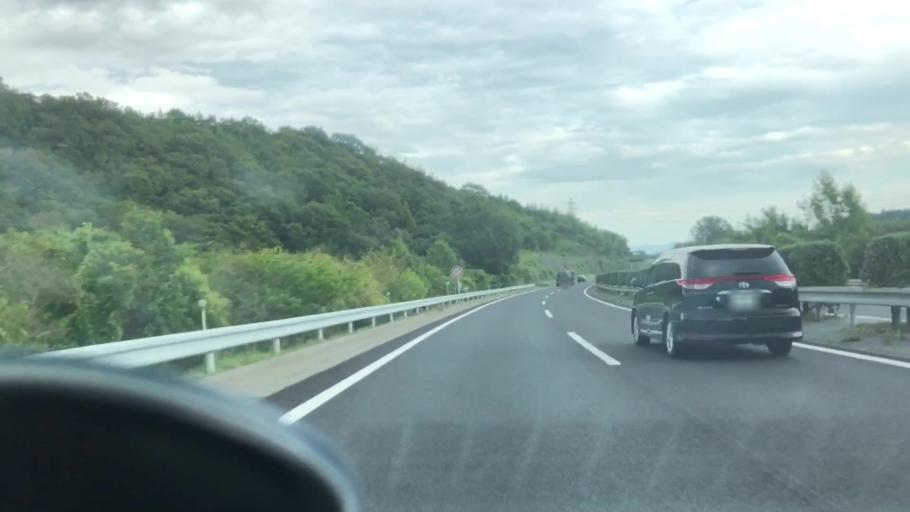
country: JP
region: Hyogo
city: Yashiro
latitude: 34.9392
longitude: 134.8790
